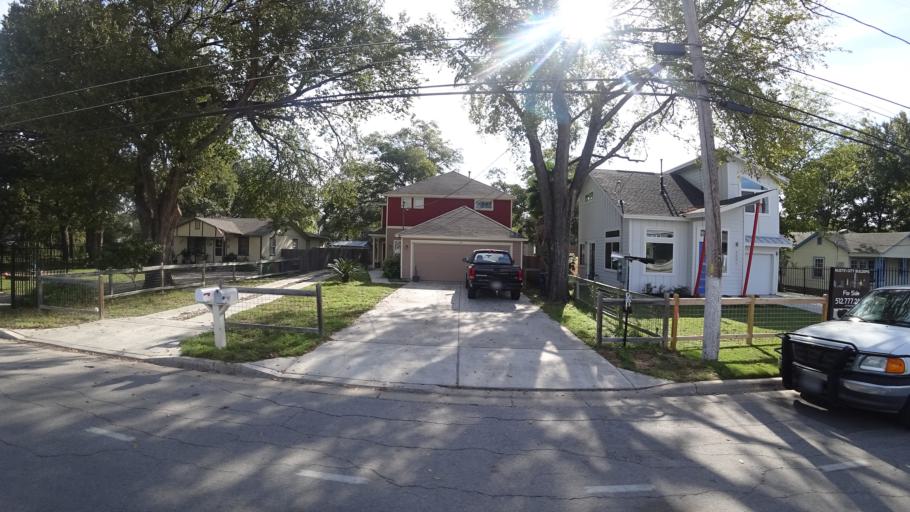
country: US
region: Texas
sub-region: Travis County
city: Austin
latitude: 30.2567
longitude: -97.7064
